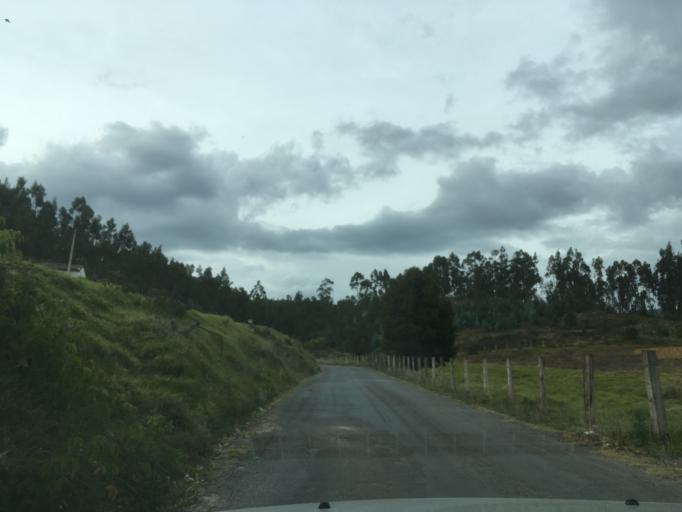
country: CO
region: Boyaca
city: Firavitoba
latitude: 5.6792
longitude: -73.0059
